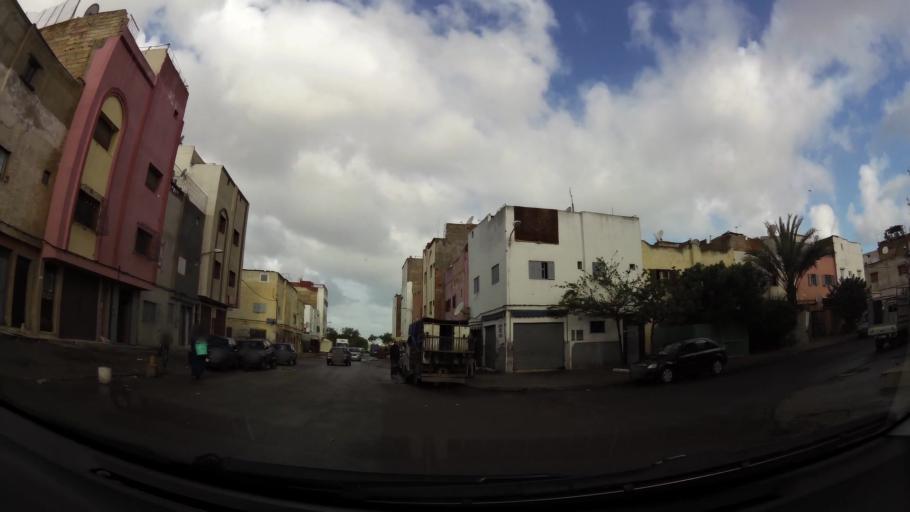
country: MA
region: Grand Casablanca
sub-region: Casablanca
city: Casablanca
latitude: 33.5577
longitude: -7.6857
